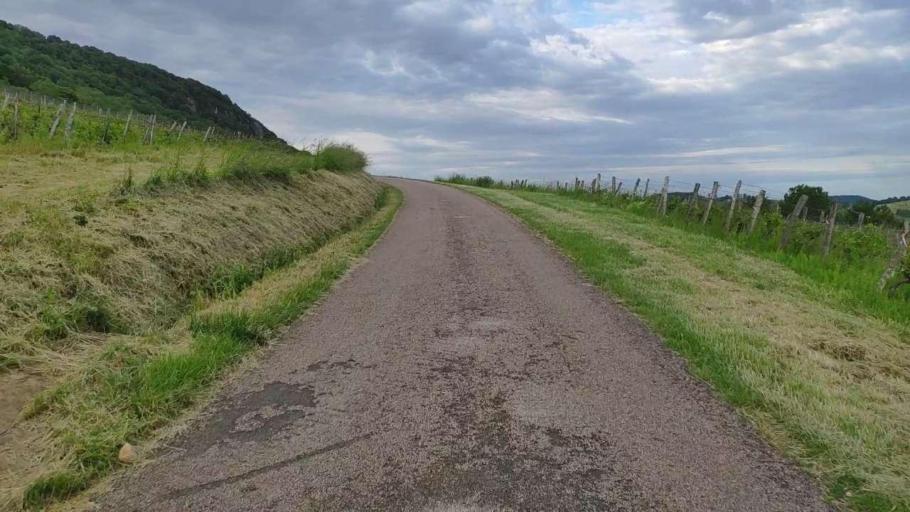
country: FR
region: Franche-Comte
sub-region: Departement du Jura
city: Perrigny
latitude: 46.7195
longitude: 5.6023
